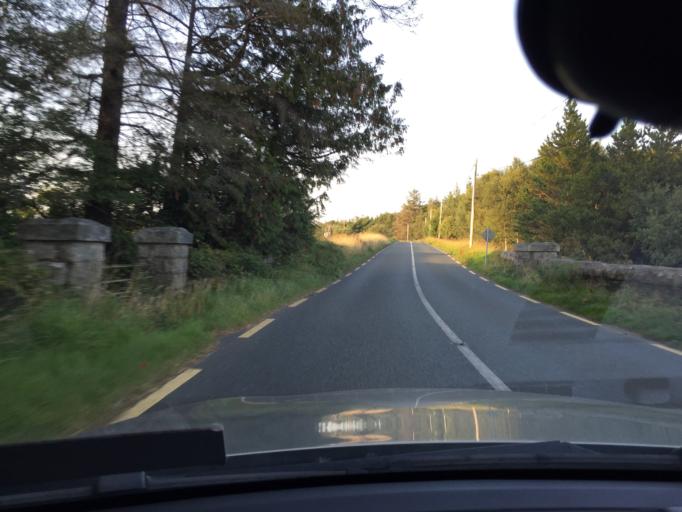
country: IE
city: Newtownmountkennedy
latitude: 53.0806
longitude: -6.2131
